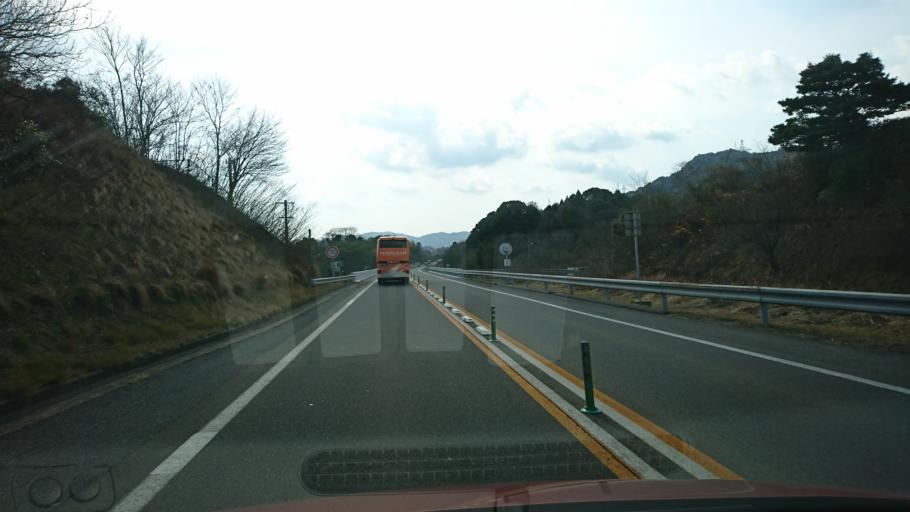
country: JP
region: Hiroshima
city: Innoshima
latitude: 34.2376
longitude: 133.0481
